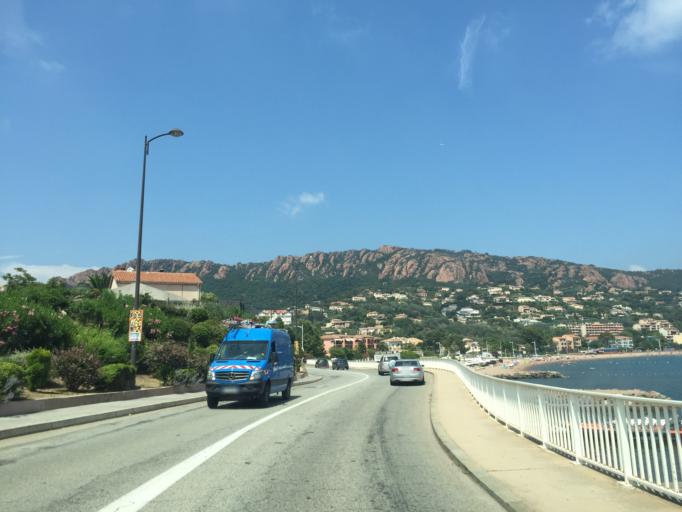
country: FR
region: Provence-Alpes-Cote d'Azur
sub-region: Departement du Var
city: Saint-Raphael
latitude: 43.4309
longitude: 6.8568
